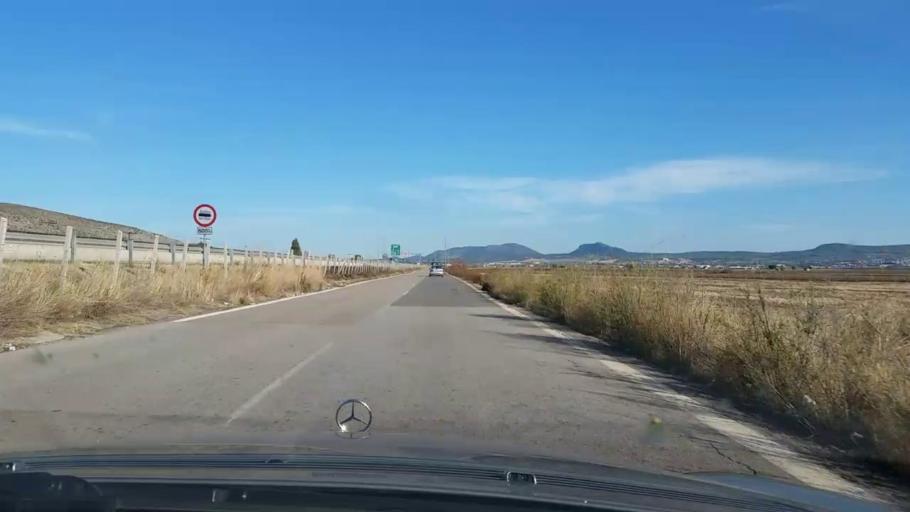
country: GR
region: Central Greece
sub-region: Nomos Voiotias
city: Thivai
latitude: 38.3729
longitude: 23.2775
